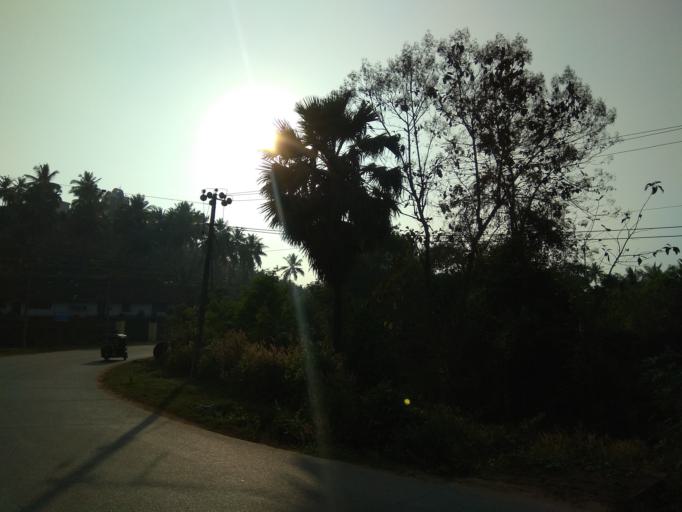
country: IN
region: Karnataka
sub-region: Dakshina Kannada
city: Mangalore
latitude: 12.9109
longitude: 74.8545
